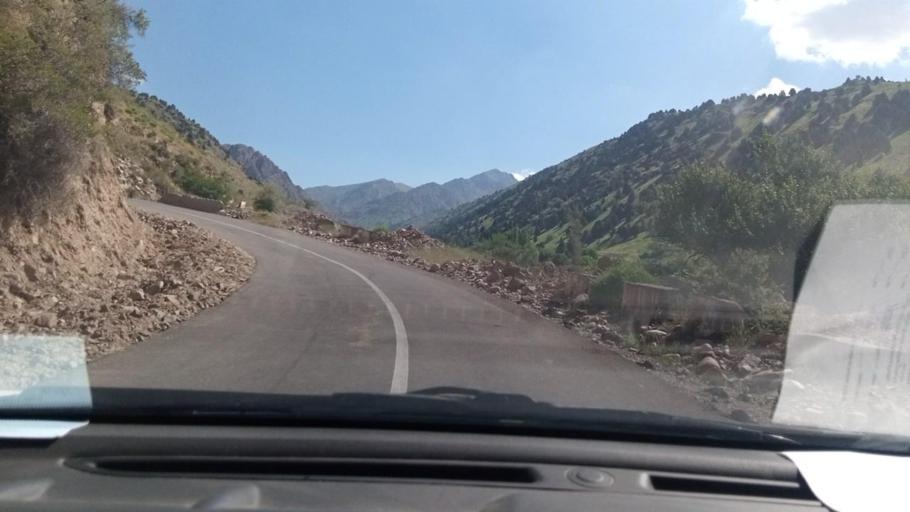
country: UZ
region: Toshkent
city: Yangiobod
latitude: 41.1256
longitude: 70.1072
